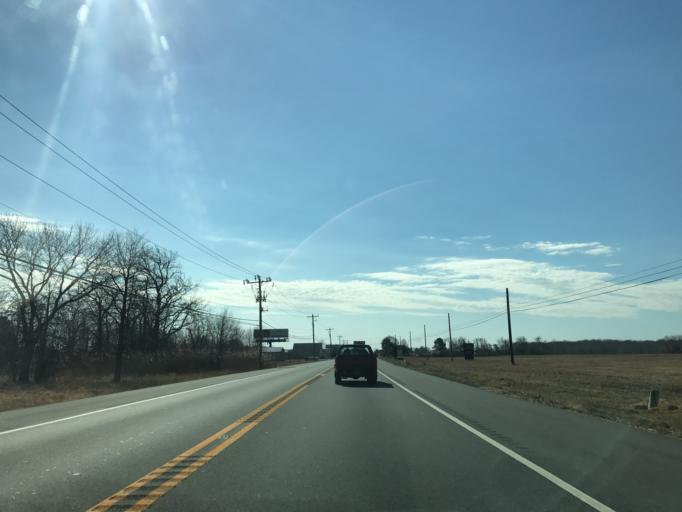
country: US
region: Delaware
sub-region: New Castle County
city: Middletown
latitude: 39.4971
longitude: -75.7138
